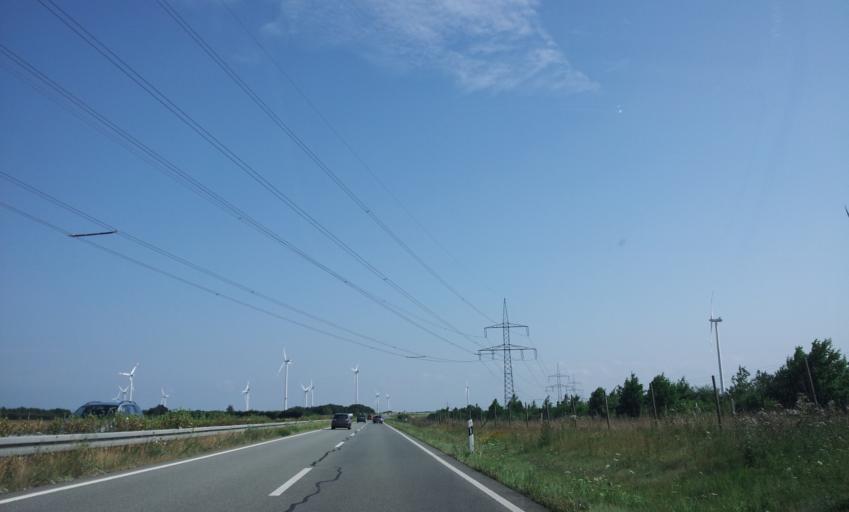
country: DE
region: Mecklenburg-Vorpommern
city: Brandshagen
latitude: 54.1838
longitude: 13.1669
